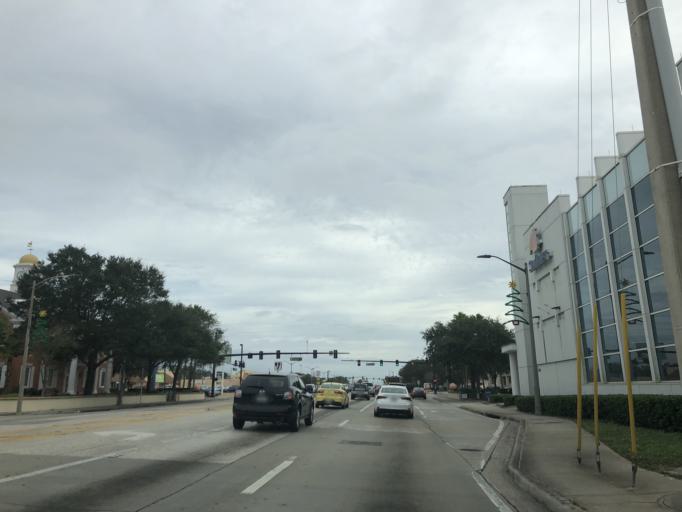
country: US
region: Florida
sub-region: Orange County
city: Orlando
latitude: 28.5531
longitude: -81.3531
